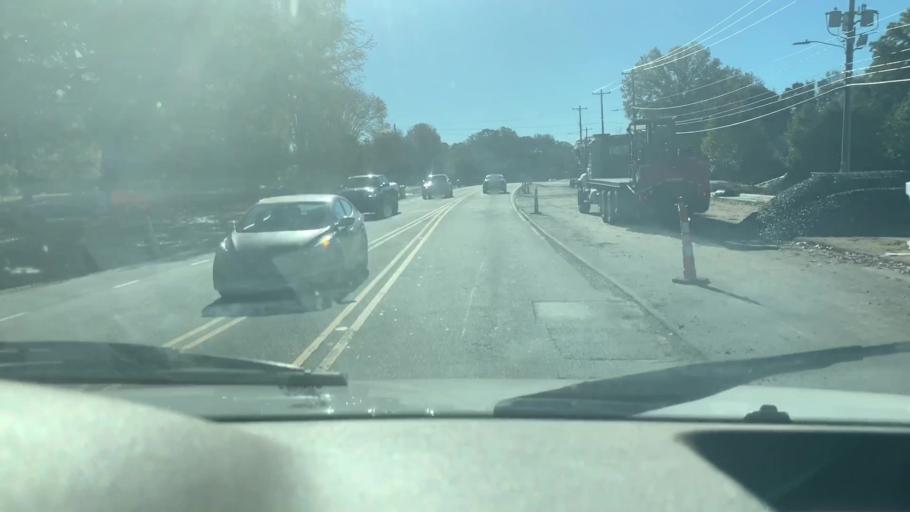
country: US
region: North Carolina
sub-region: Mecklenburg County
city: Charlotte
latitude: 35.3035
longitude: -80.8572
